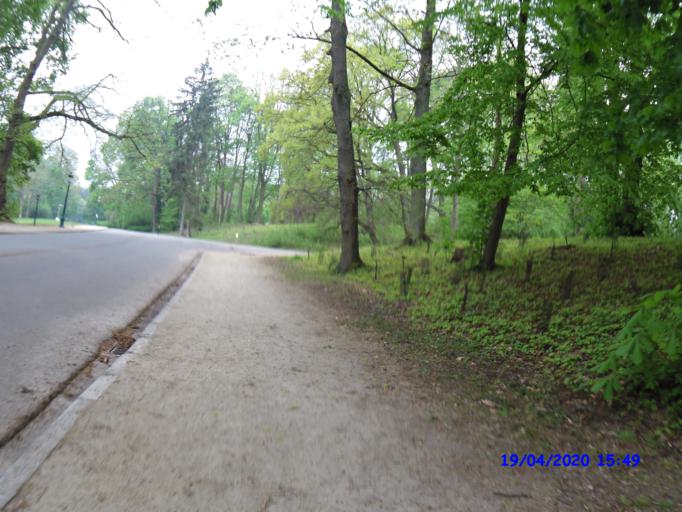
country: BE
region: Flanders
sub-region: Provincie Vlaams-Brabant
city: Kraainem
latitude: 50.8307
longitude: 4.4297
